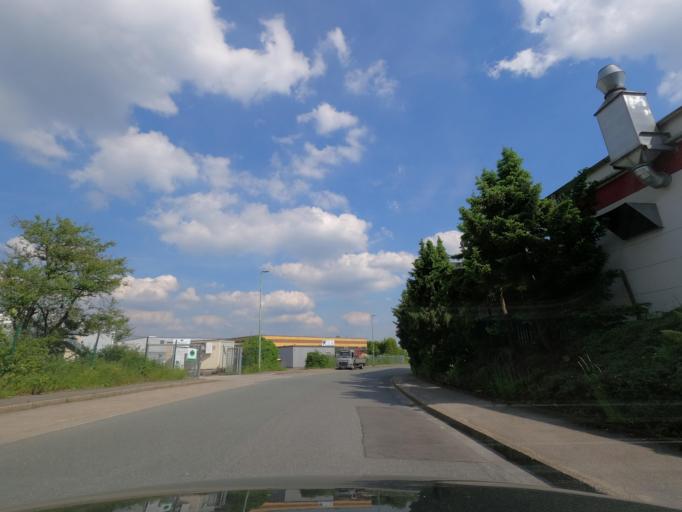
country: DE
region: North Rhine-Westphalia
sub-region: Regierungsbezirk Arnsberg
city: Luedenscheid
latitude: 51.2492
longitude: 7.6084
